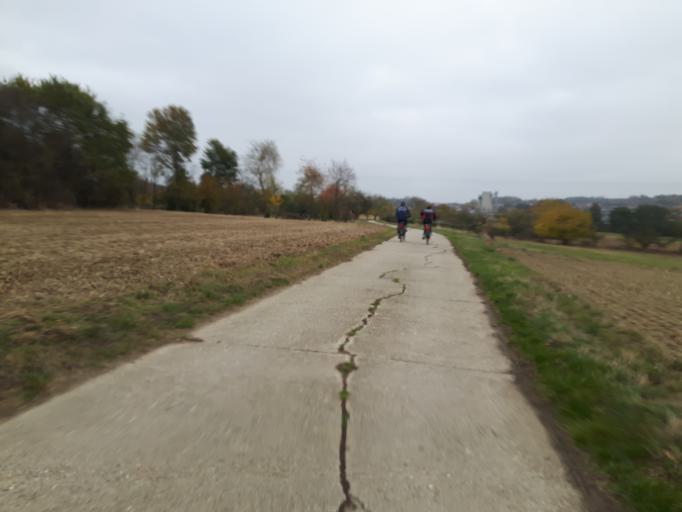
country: DE
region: Baden-Wuerttemberg
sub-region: Karlsruhe Region
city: Ostringen
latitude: 49.2179
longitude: 8.6887
